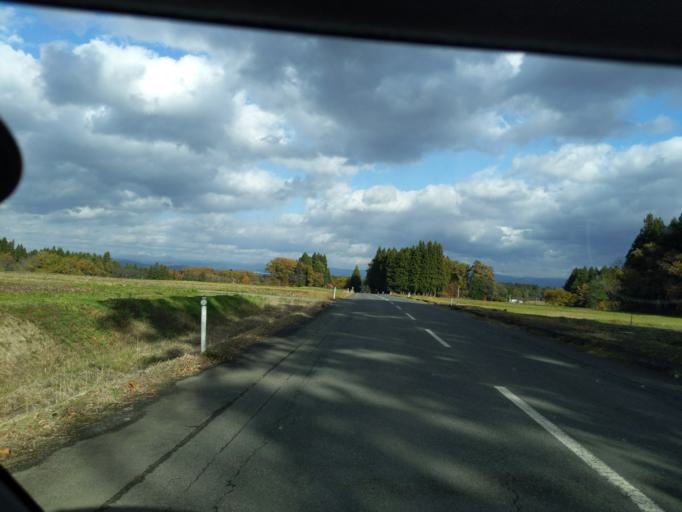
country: JP
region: Iwate
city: Mizusawa
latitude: 39.1140
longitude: 141.0342
